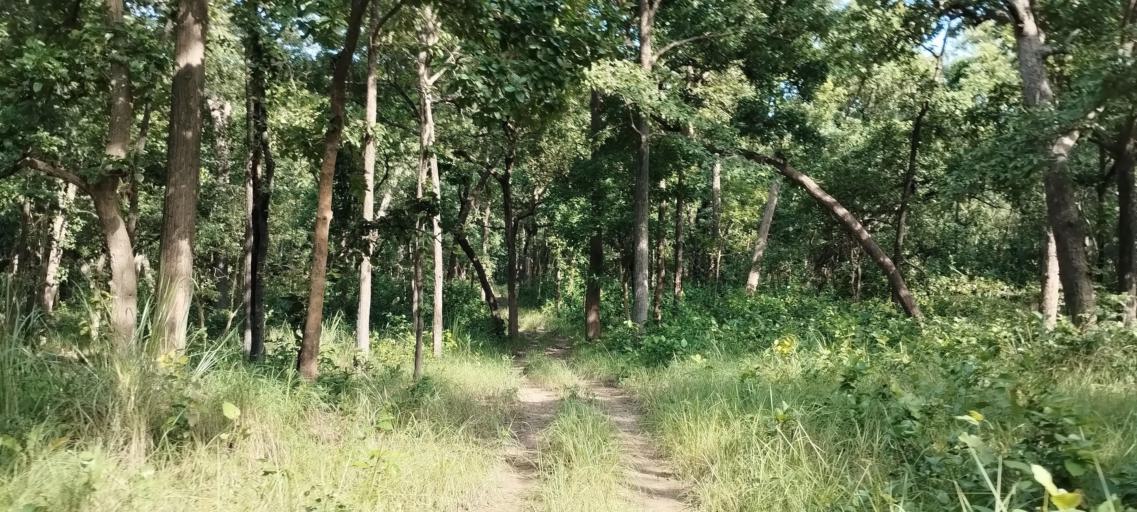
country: NP
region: Far Western
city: Tikapur
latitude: 28.5557
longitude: 81.2688
